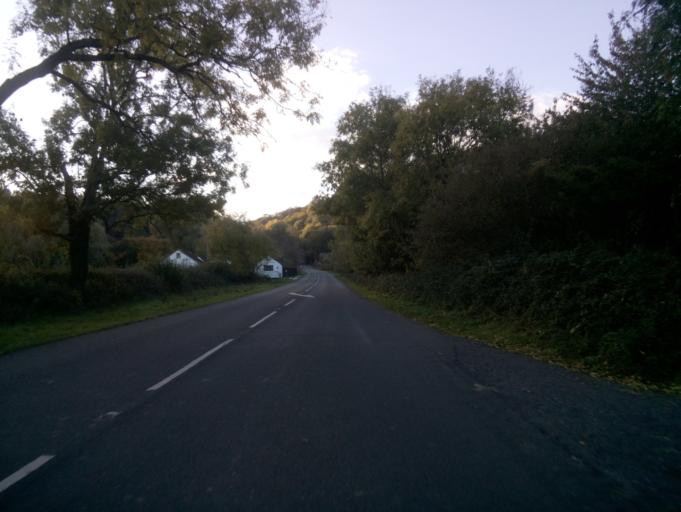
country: GB
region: England
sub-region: Herefordshire
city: Donnington
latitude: 52.0292
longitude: -2.3421
